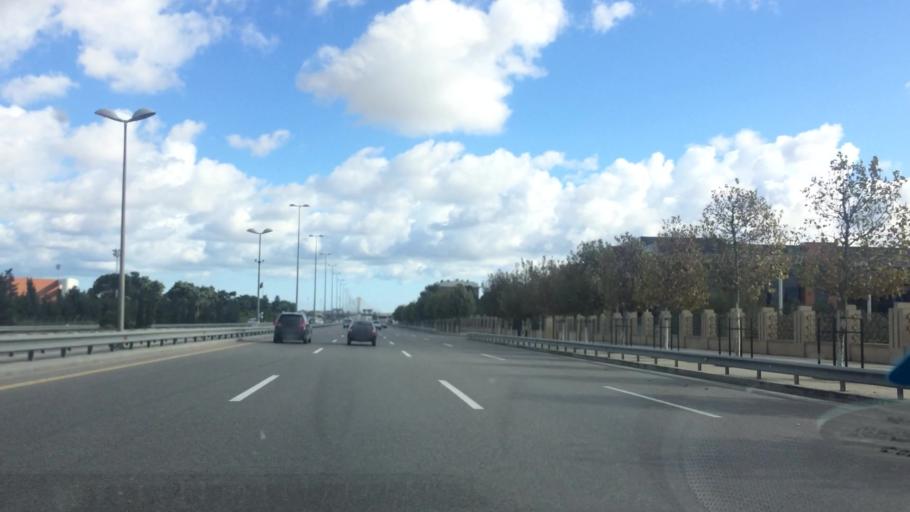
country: AZ
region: Baki
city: Biny Selo
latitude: 40.4535
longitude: 50.0649
